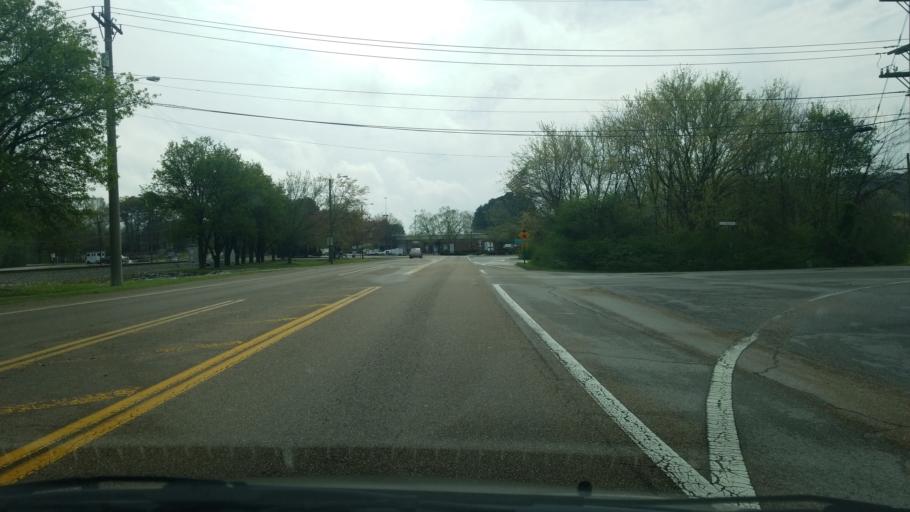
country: US
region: Tennessee
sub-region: Hamilton County
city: Collegedale
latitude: 35.0533
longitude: -85.0502
